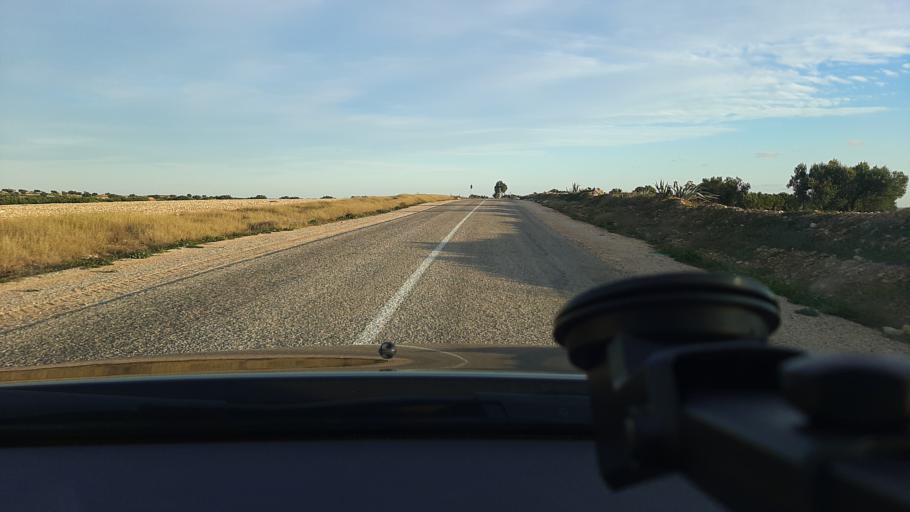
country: TN
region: Safaqis
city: Sfax
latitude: 34.9549
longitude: 10.5479
